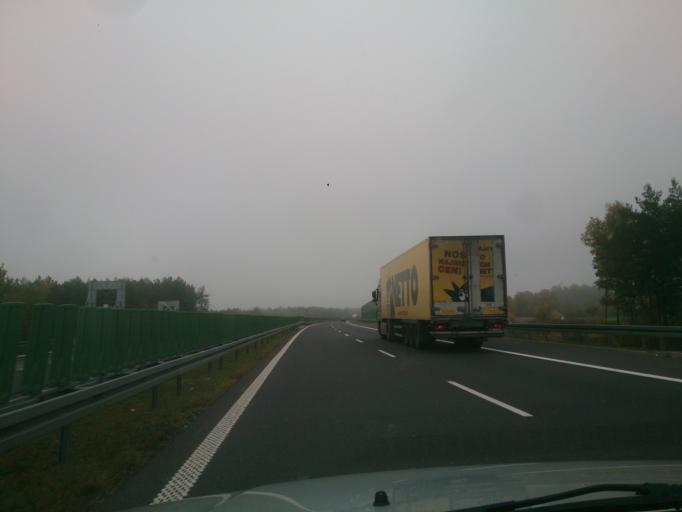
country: PL
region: Kujawsko-Pomorskie
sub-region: Powiat swiecki
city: Warlubie
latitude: 53.6543
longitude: 18.6389
